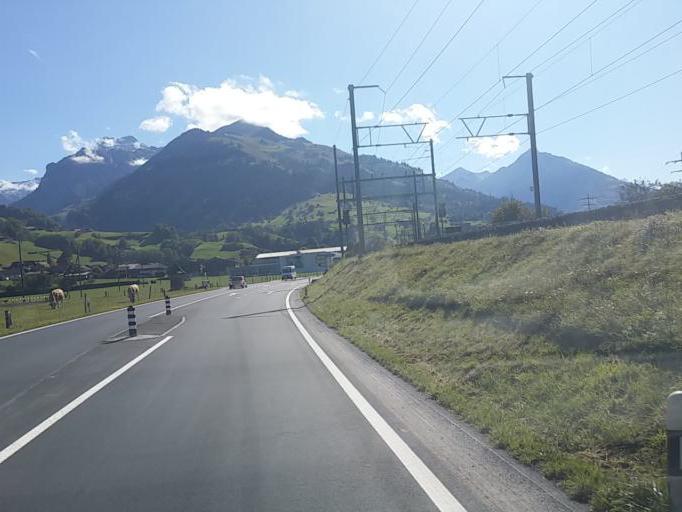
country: CH
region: Bern
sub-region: Frutigen-Niedersimmental District
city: Aeschi
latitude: 46.6310
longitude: 7.6916
